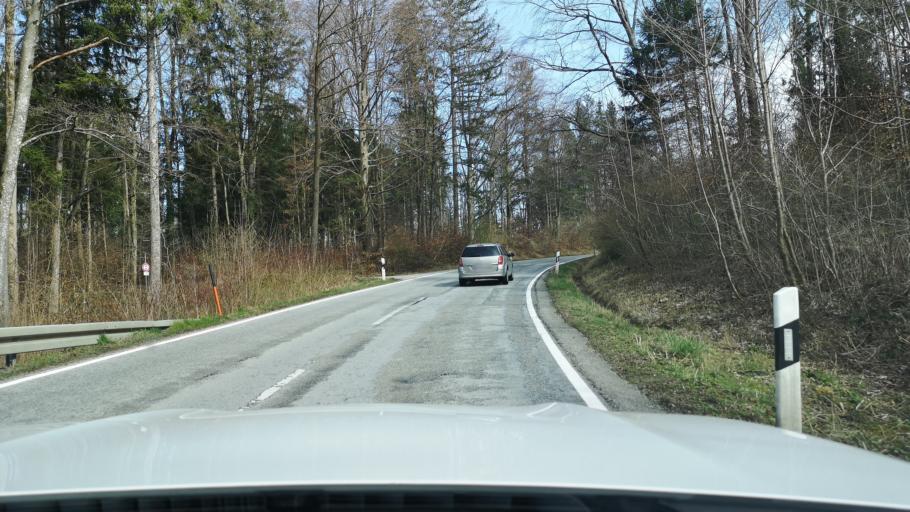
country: DE
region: Bavaria
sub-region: Upper Bavaria
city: Isen
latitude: 48.2156
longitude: 12.0337
